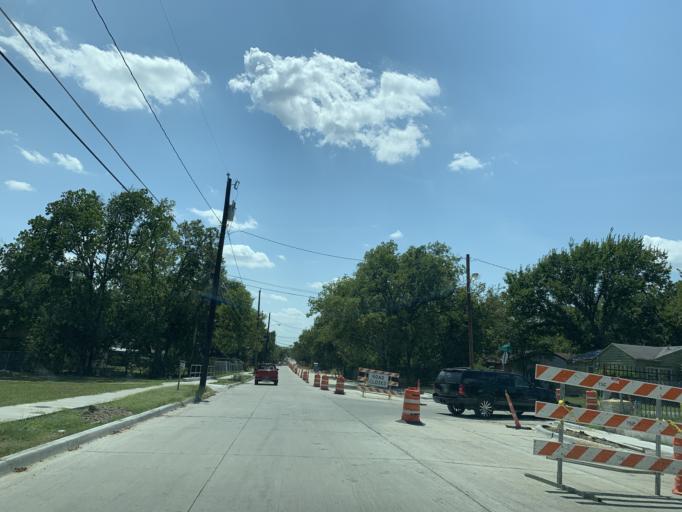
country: US
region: Texas
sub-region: Dallas County
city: Dallas
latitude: 32.7127
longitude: -96.7696
